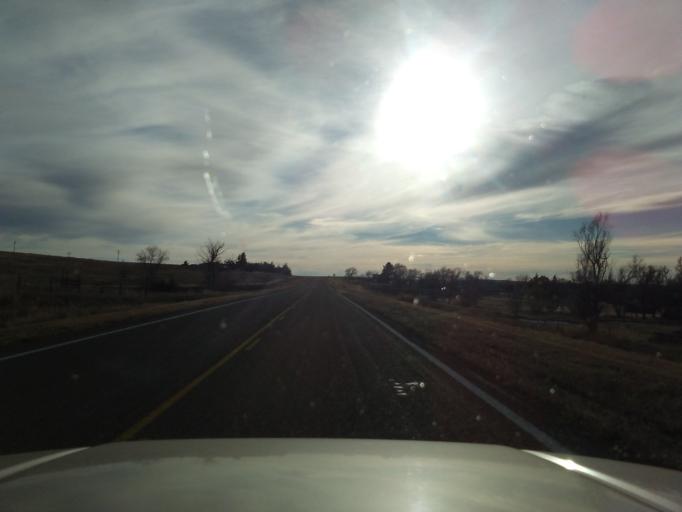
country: US
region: Kansas
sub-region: Norton County
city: Norton
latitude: 39.7380
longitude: -100.1733
